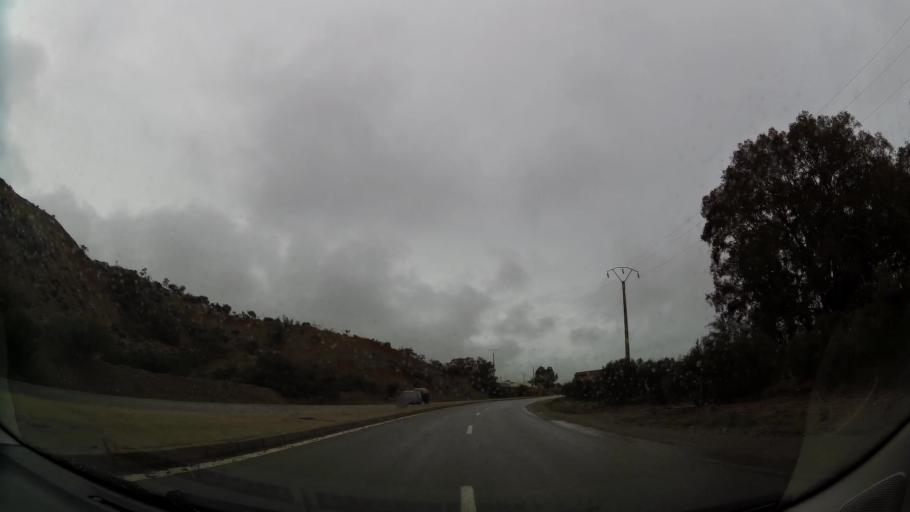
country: MA
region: Taza-Al Hoceima-Taounate
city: Imzourene
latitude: 35.1843
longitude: -3.8821
